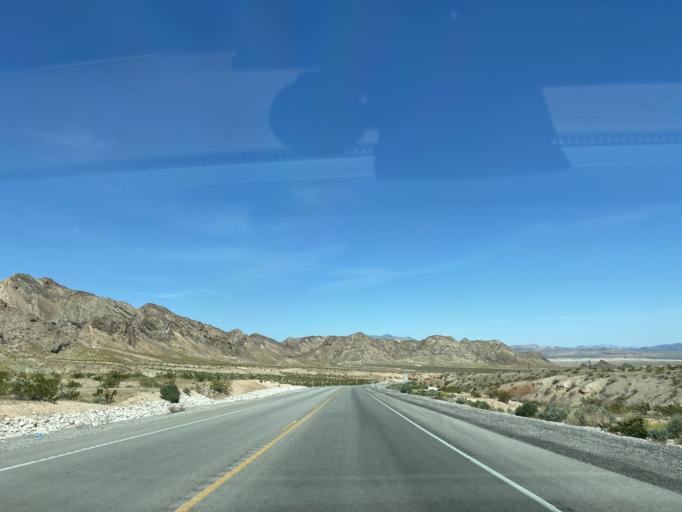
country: US
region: Nevada
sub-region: Clark County
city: Nellis Air Force Base
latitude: 36.2047
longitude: -114.9685
